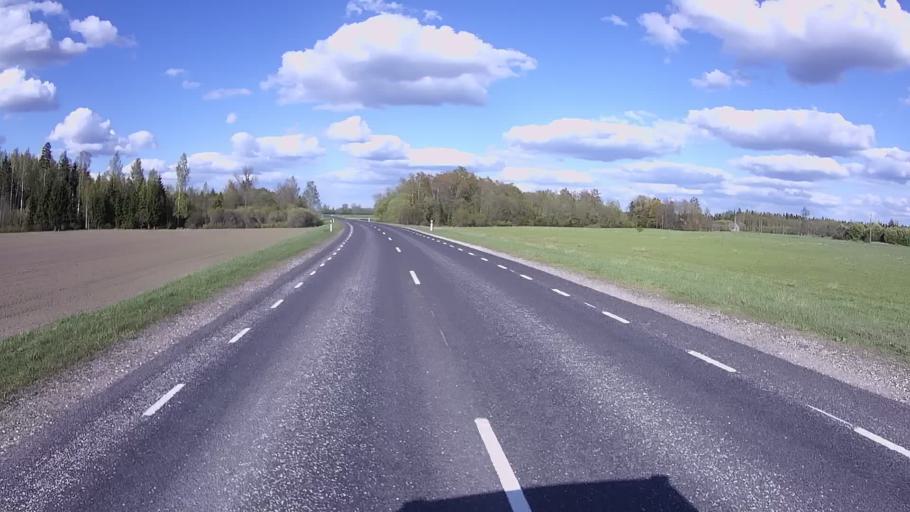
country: EE
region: Jogevamaa
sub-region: Poltsamaa linn
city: Poltsamaa
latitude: 58.7115
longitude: 26.1743
